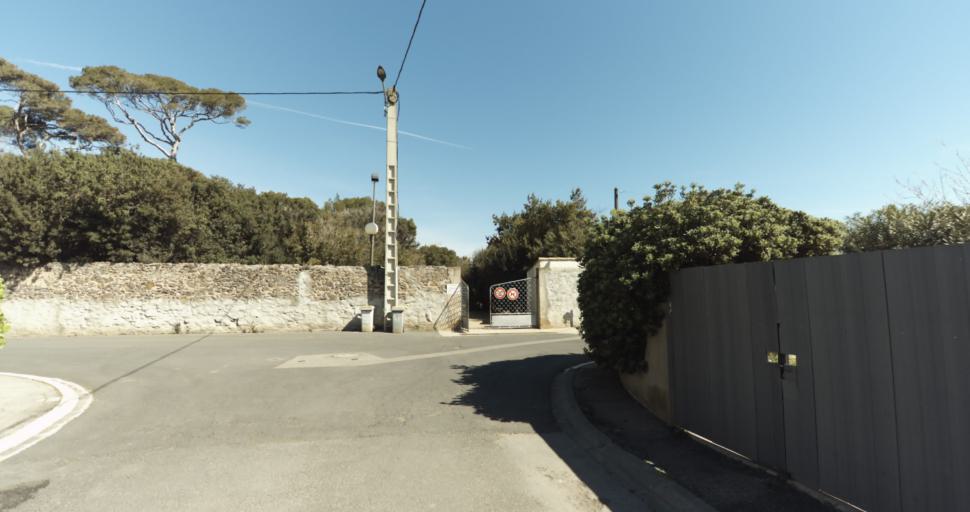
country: FR
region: Languedoc-Roussillon
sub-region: Departement de l'Herault
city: Marseillan
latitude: 43.3563
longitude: 3.5318
